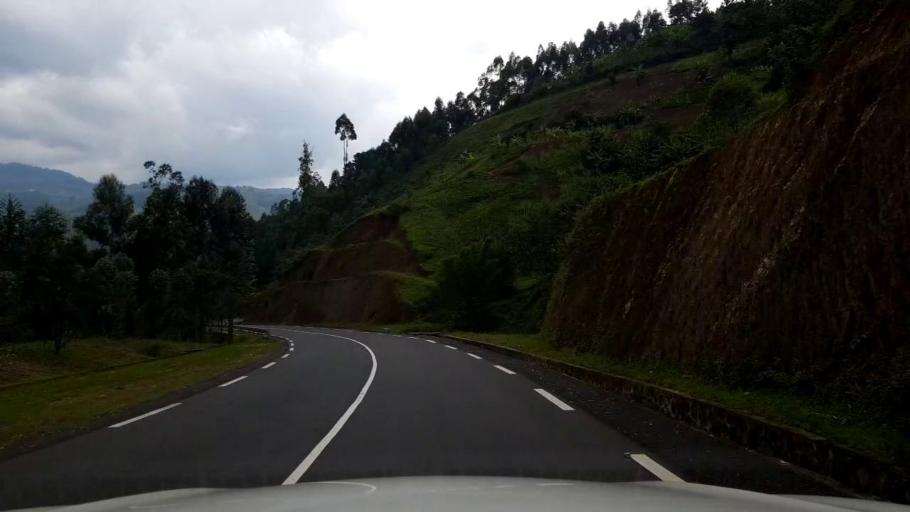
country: RW
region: Western Province
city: Kibuye
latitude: -1.9080
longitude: 29.3626
